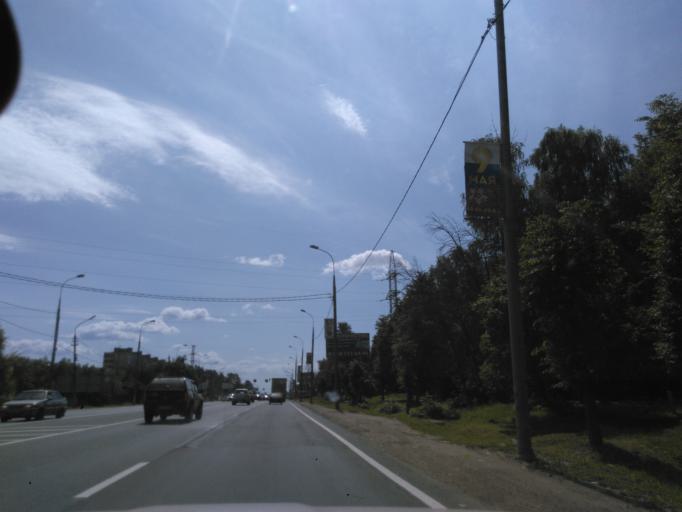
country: RU
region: Moskovskaya
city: Solnechnogorsk
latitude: 56.1807
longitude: 36.9884
